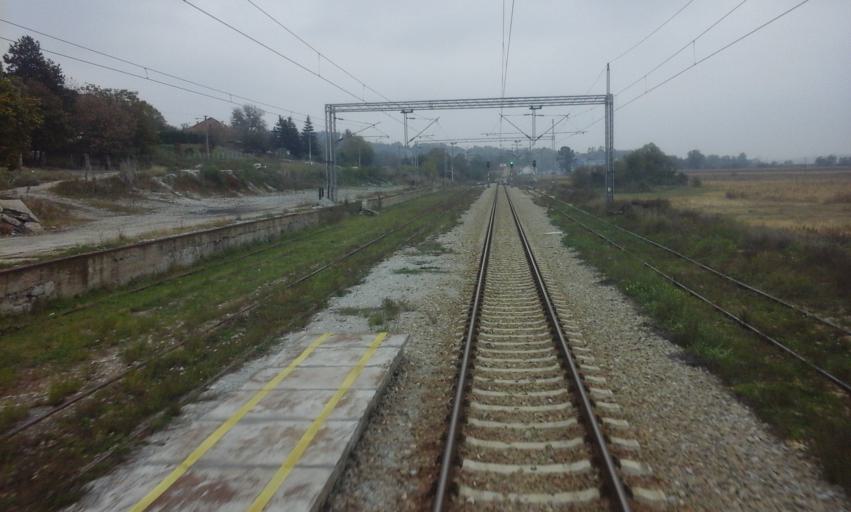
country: RS
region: Central Serbia
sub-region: Belgrade
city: Mladenovac
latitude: 44.4805
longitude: 20.6604
